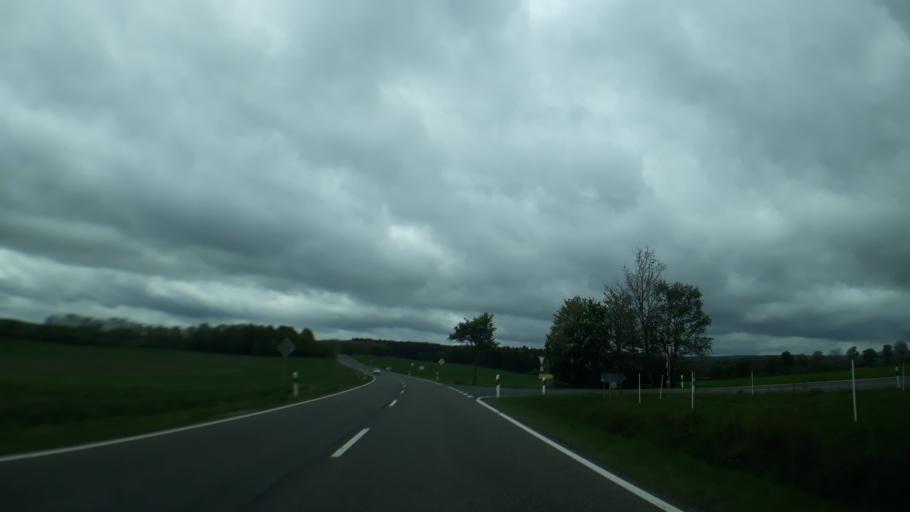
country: DE
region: North Rhine-Westphalia
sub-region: Regierungsbezirk Koln
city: Kall
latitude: 50.5320
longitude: 6.5871
